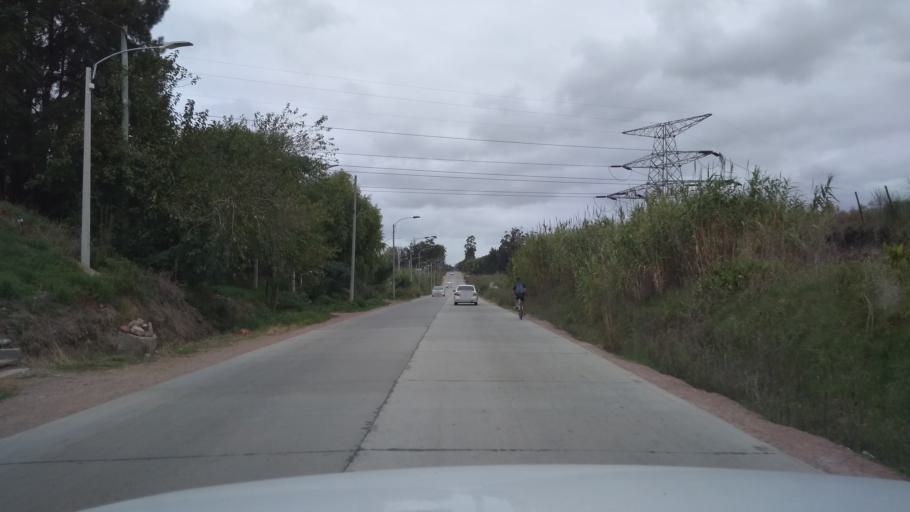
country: UY
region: Canelones
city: Toledo
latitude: -34.7912
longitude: -56.1465
